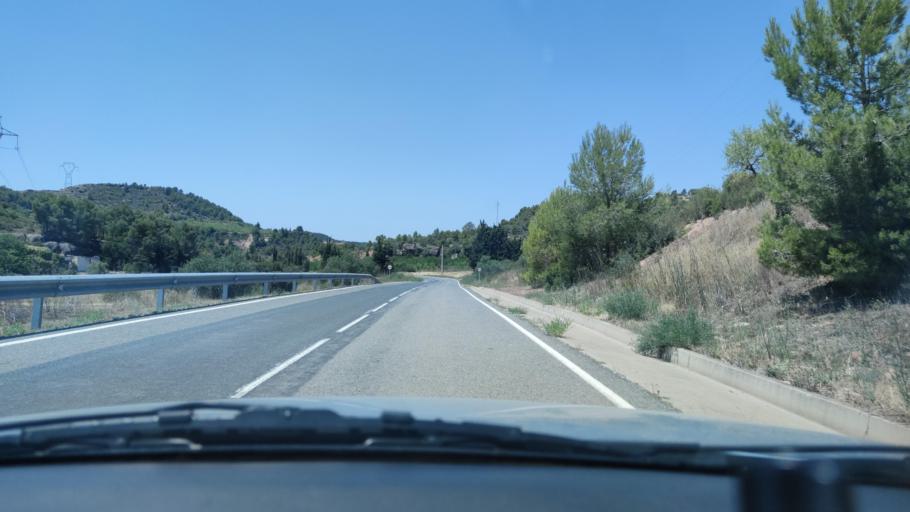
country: ES
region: Catalonia
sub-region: Provincia de Lleida
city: Juncosa
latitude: 41.3914
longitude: 0.7360
